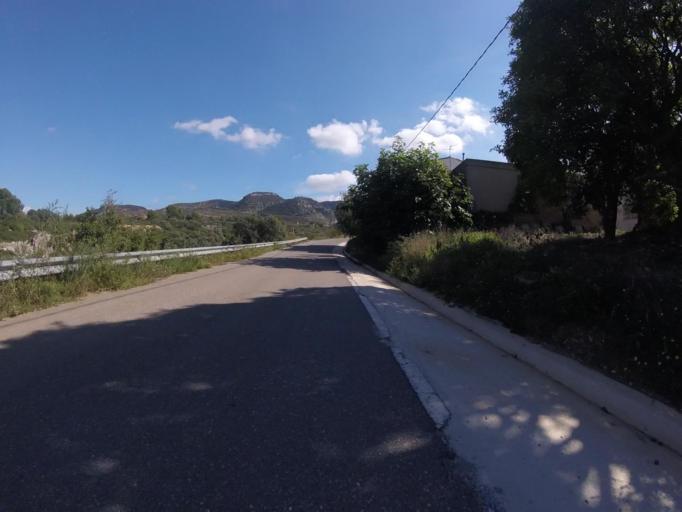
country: ES
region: Valencia
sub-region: Provincia de Castello
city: Sierra-Engarceran
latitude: 40.2964
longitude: -0.0431
